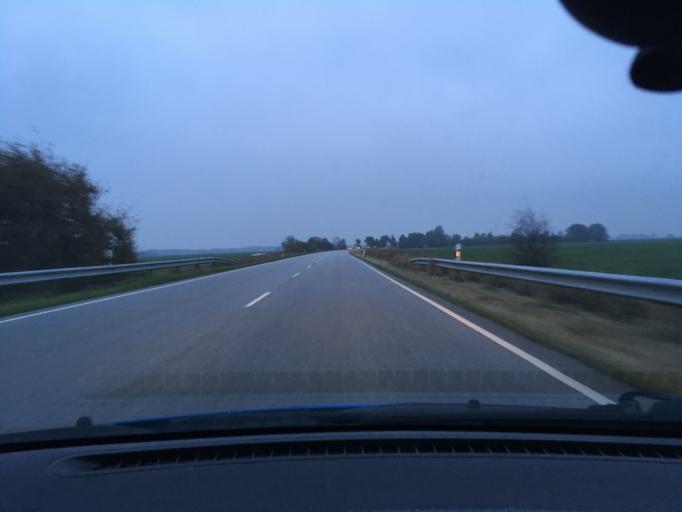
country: DE
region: Schleswig-Holstein
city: Lohe-Rickelshof
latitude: 54.2130
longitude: 9.0466
